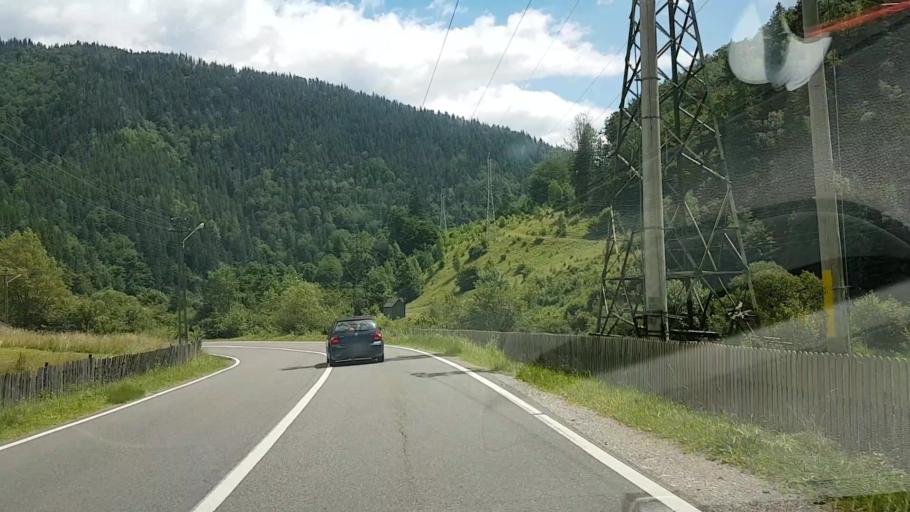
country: RO
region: Suceava
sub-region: Comuna Crucea
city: Crucea
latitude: 47.2823
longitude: 25.6408
